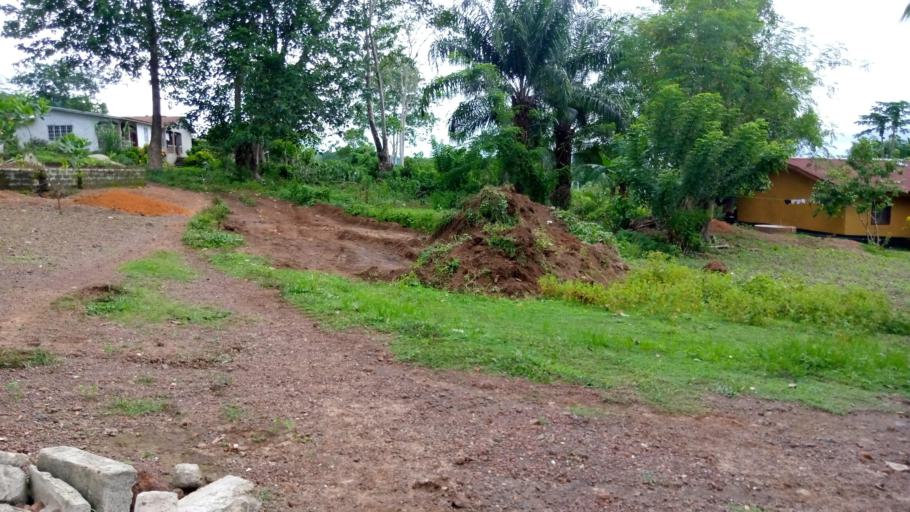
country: SL
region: Southern Province
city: Moyamba
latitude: 8.1623
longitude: -12.4428
